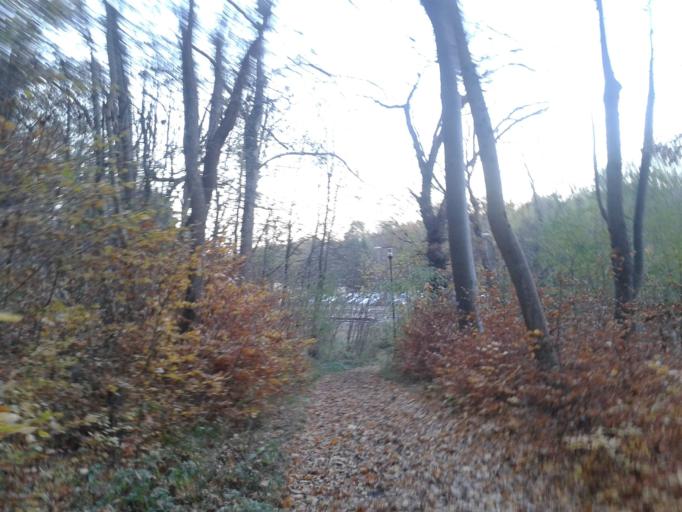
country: DE
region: Hesse
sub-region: Regierungsbezirk Darmstadt
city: Schluchtern
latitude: 50.3404
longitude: 9.5067
